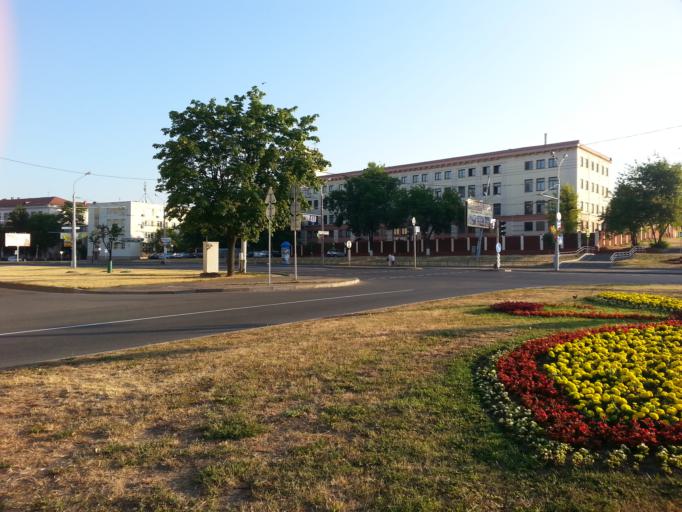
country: BY
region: Minsk
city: Minsk
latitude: 53.8722
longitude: 27.6389
